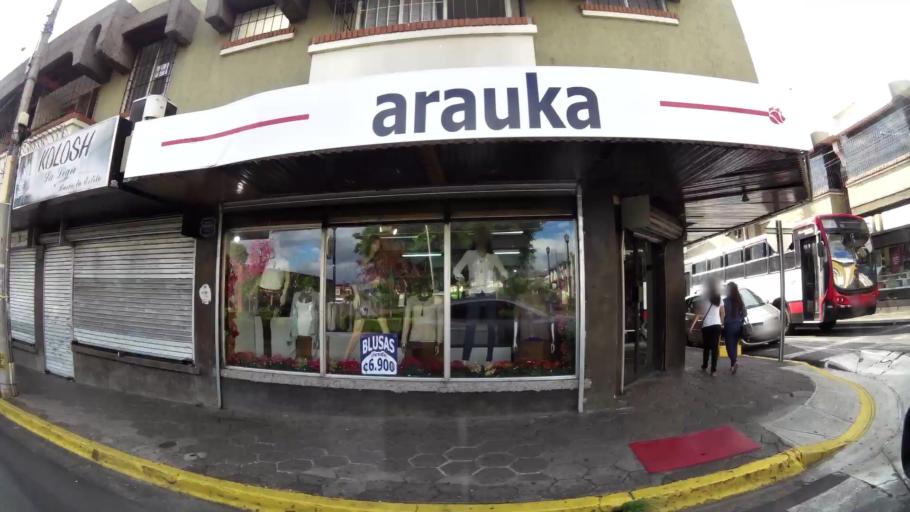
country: CR
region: Alajuela
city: Alajuela
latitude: 10.0151
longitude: -84.2140
